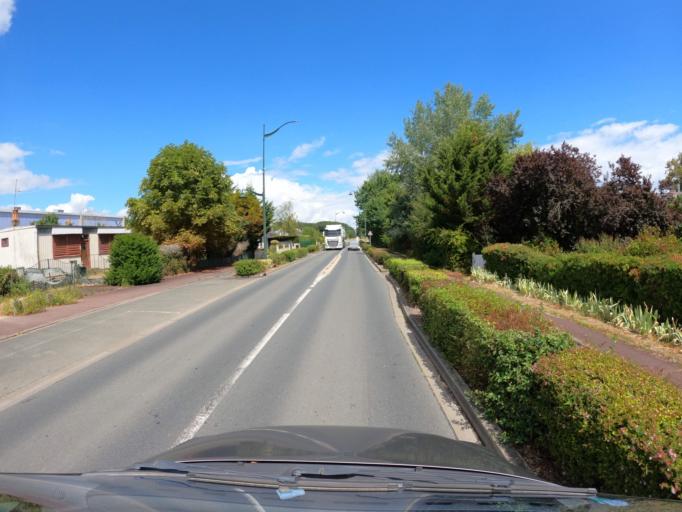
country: FR
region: Pays de la Loire
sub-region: Departement de Maine-et-Loire
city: Feneu
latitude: 47.5746
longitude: -0.5931
